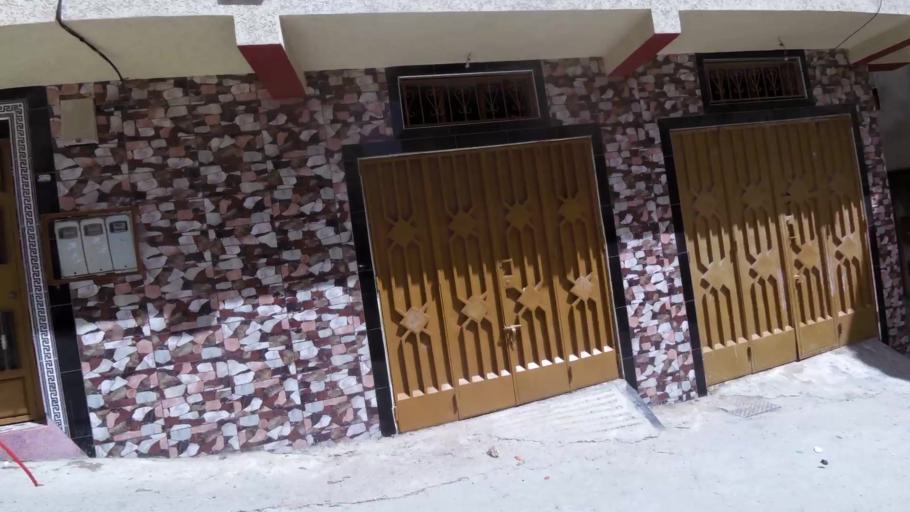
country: MA
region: Tanger-Tetouan
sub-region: Tanger-Assilah
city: Tangier
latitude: 35.7308
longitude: -5.8092
